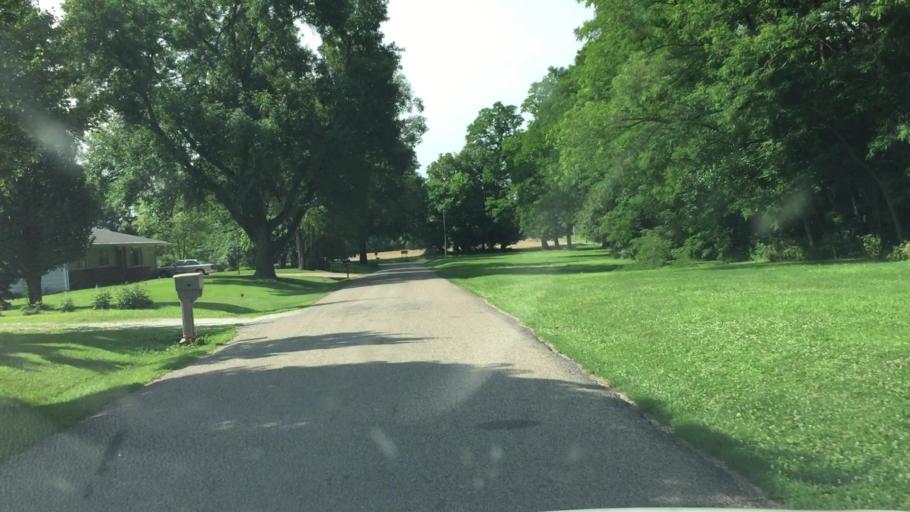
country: US
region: Illinois
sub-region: Hancock County
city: Nauvoo
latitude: 40.5443
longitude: -91.3755
